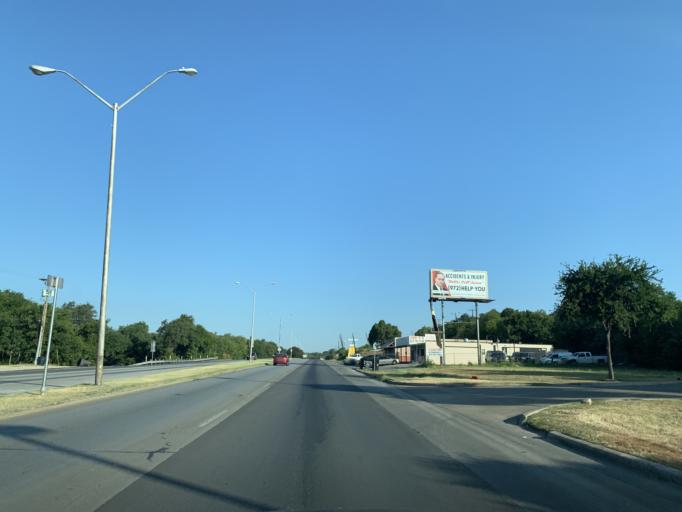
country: US
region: Texas
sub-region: Tarrant County
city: River Oaks
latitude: 32.7894
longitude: -97.3878
